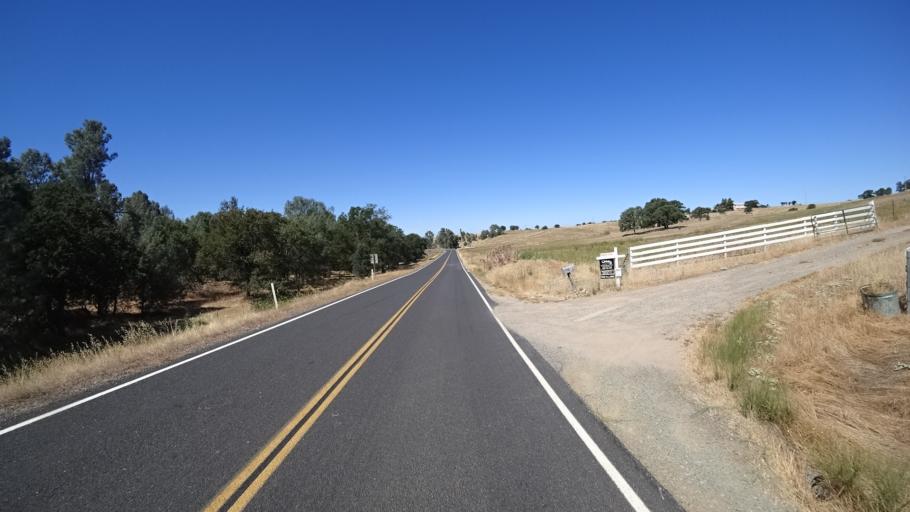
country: US
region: California
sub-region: Calaveras County
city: Rancho Calaveras
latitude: 38.0674
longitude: -120.8661
